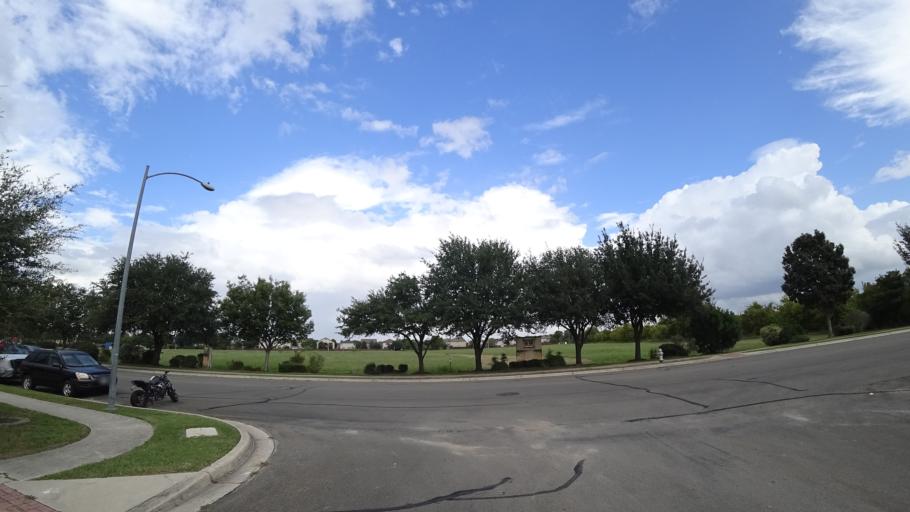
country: US
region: Texas
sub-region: Travis County
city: Onion Creek
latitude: 30.1555
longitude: -97.7427
